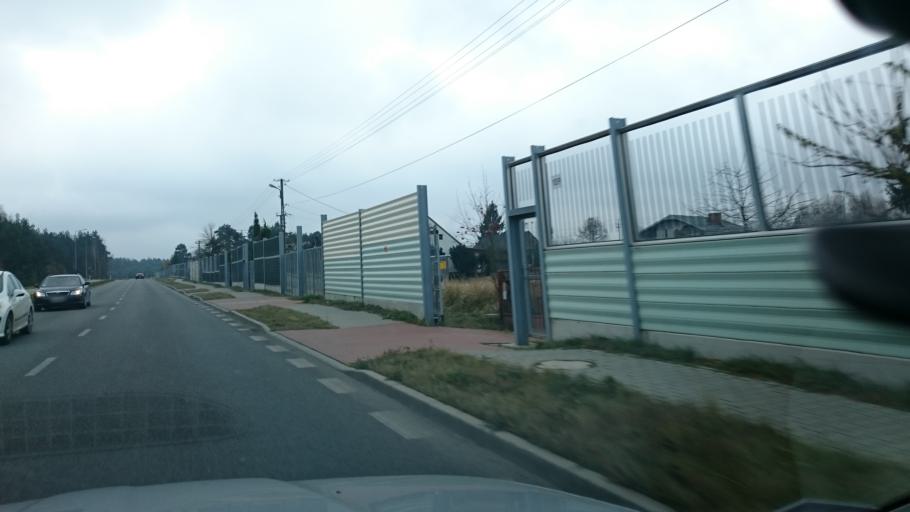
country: PL
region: Swietokrzyskie
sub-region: Powiat konecki
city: Konskie
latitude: 51.1562
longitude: 20.3652
